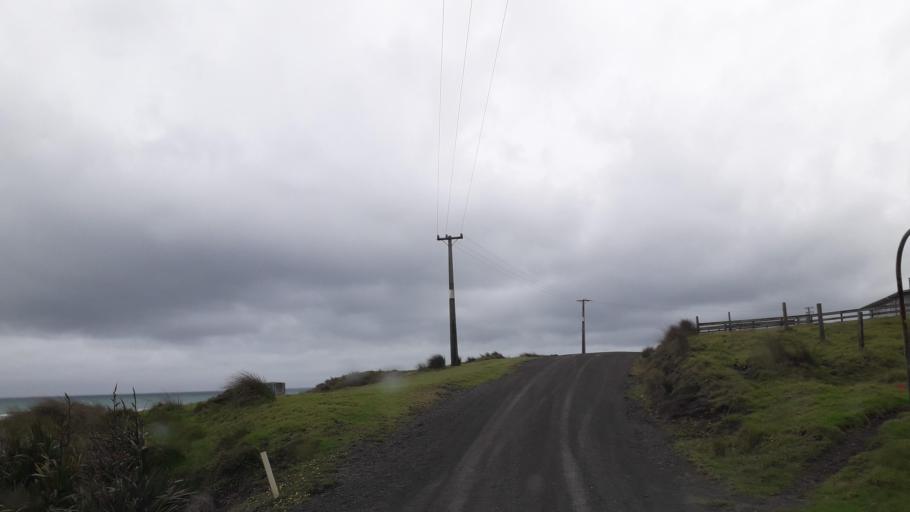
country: NZ
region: Northland
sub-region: Far North District
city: Ahipara
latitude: -35.4300
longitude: 173.2725
